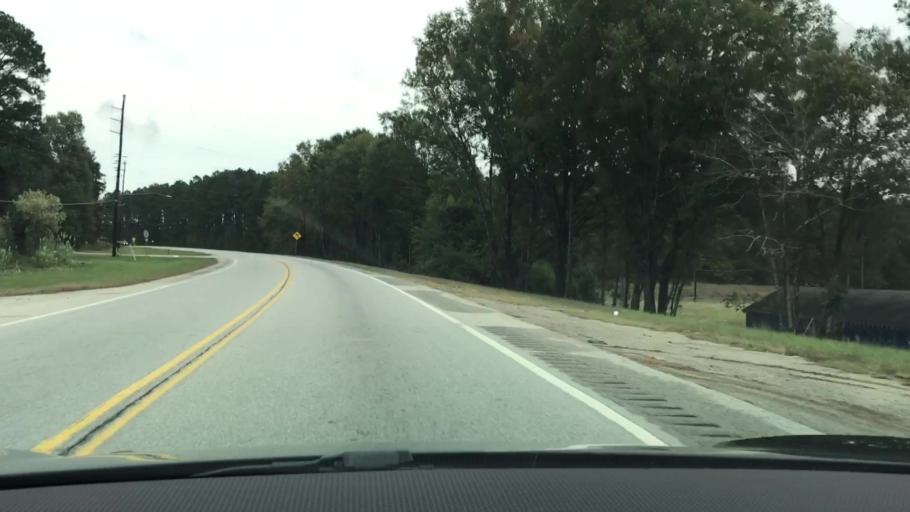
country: US
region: Georgia
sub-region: Warren County
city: Warrenton
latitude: 33.4009
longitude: -82.6670
